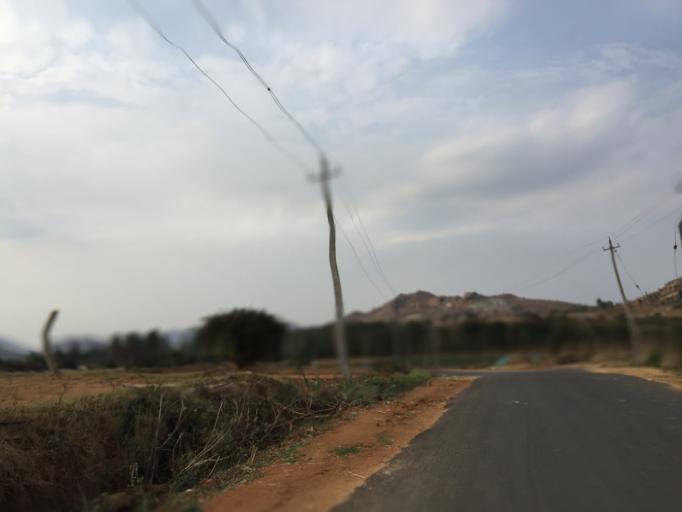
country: IN
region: Karnataka
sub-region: Chikkaballapur
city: Gudibanda
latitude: 13.5704
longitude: 77.7295
